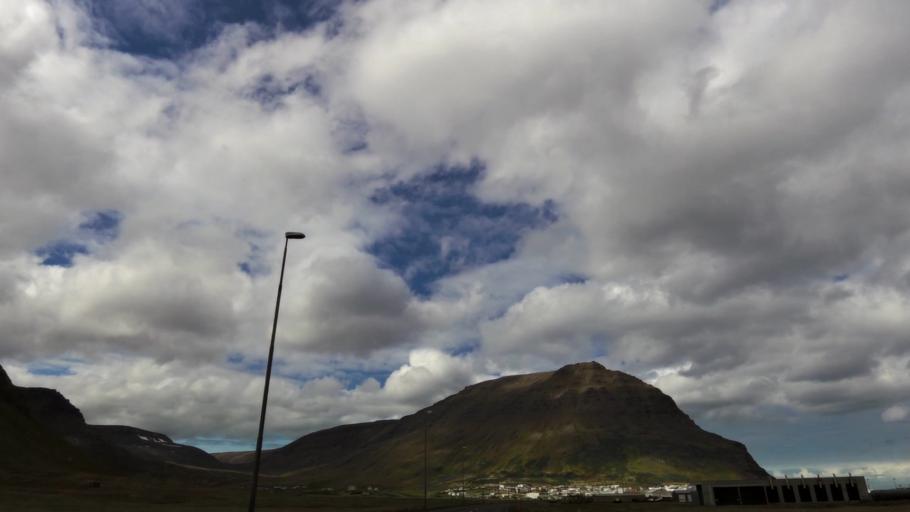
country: IS
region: Westfjords
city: Isafjoerdur
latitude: 66.1477
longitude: -23.2410
